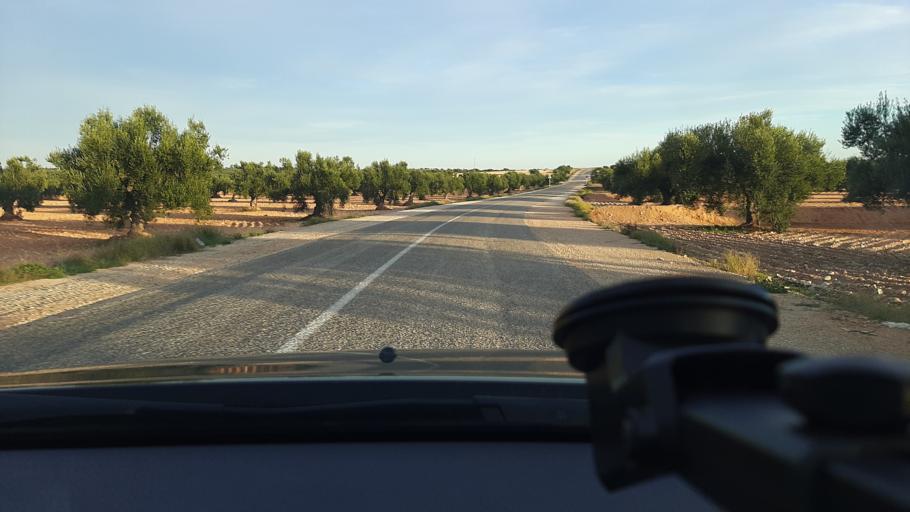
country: TN
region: Safaqis
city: Sfax
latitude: 34.9572
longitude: 10.5422
